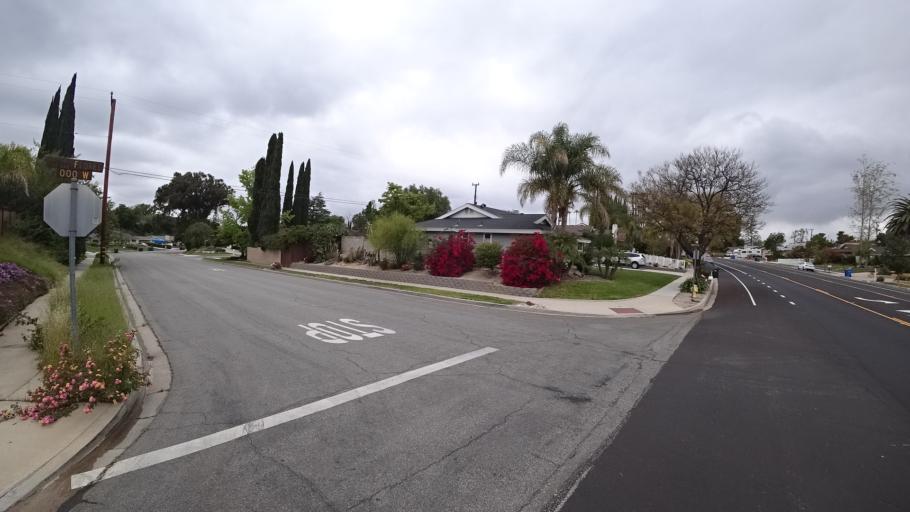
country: US
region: California
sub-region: Ventura County
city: Thousand Oaks
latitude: 34.2102
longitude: -118.8751
